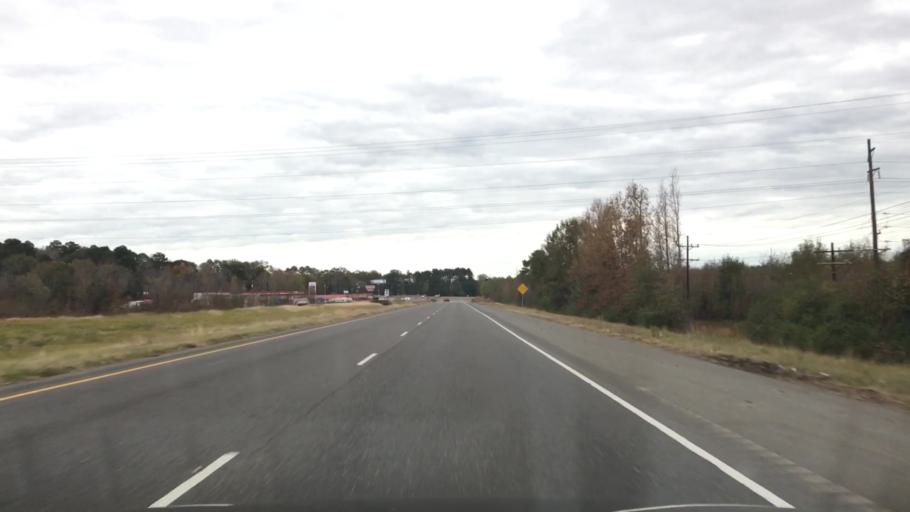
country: US
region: Louisiana
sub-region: Vernon Parish
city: New Llano
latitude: 31.1061
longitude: -93.2706
